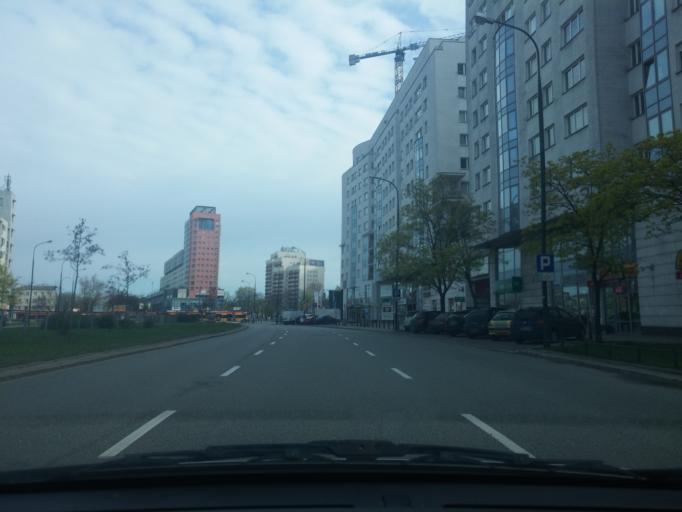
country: PL
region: Masovian Voivodeship
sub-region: Warszawa
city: Praga Poludnie
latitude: 52.2428
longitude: 21.0842
